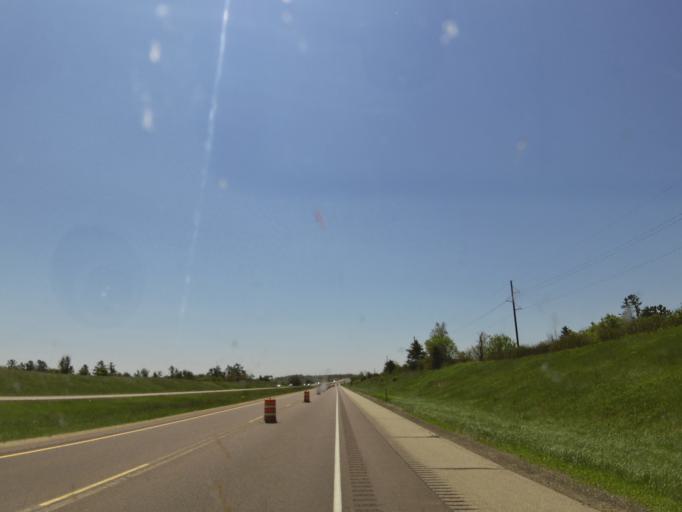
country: US
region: Wisconsin
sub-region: Monroe County
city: Tomah
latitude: 44.0653
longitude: -90.5197
